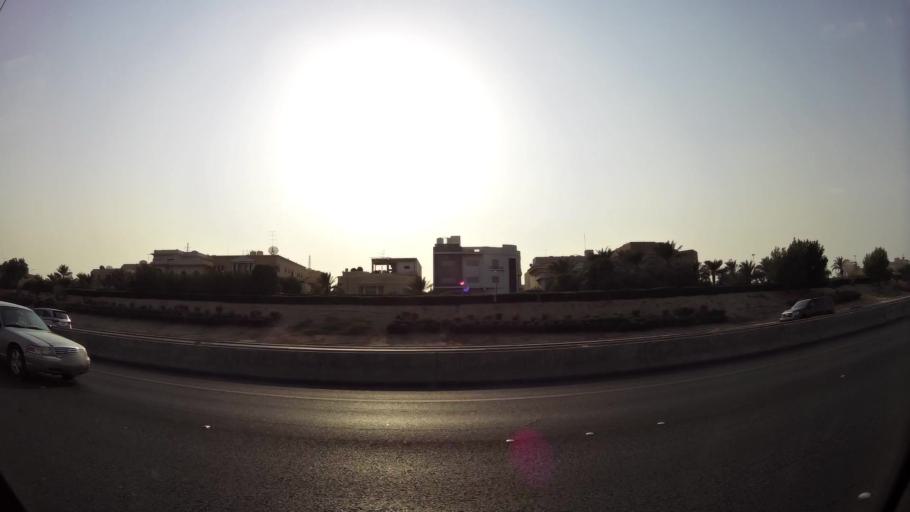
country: KW
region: Muhafazat Hawalli
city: Hawalli
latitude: 29.3138
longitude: 48.0193
